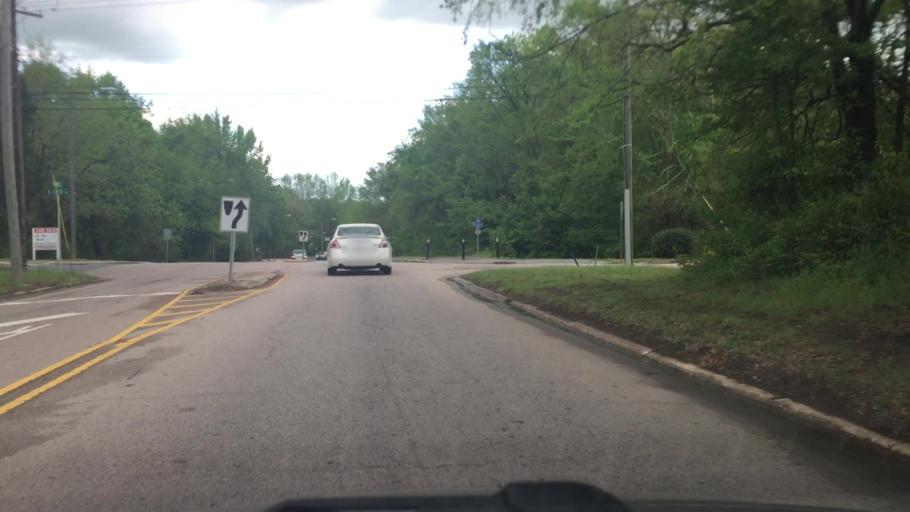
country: US
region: North Carolina
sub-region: Rowan County
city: Salisbury
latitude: 35.6782
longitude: -80.4888
